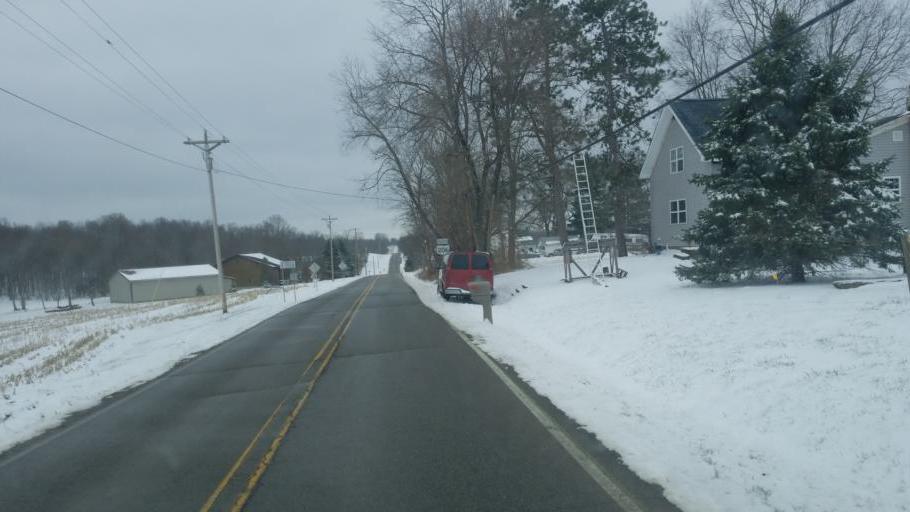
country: US
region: Ohio
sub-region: Knox County
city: Oak Hill
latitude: 40.4178
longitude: -82.1381
